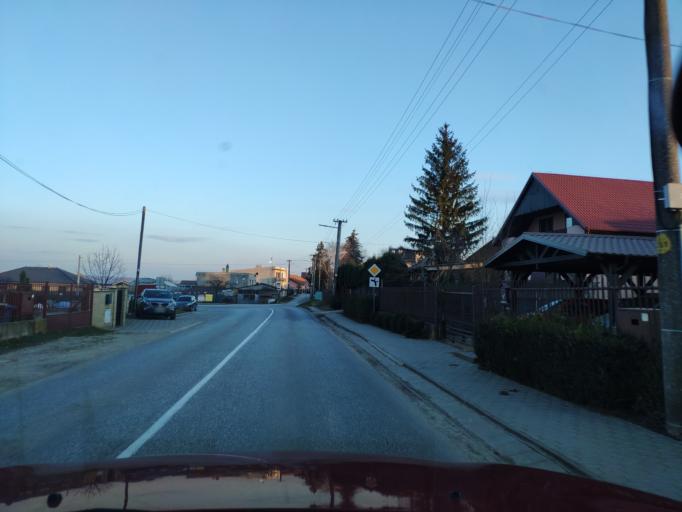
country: SK
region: Nitriansky
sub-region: Okres Nitra
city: Nitra
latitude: 48.2405
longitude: 18.0245
